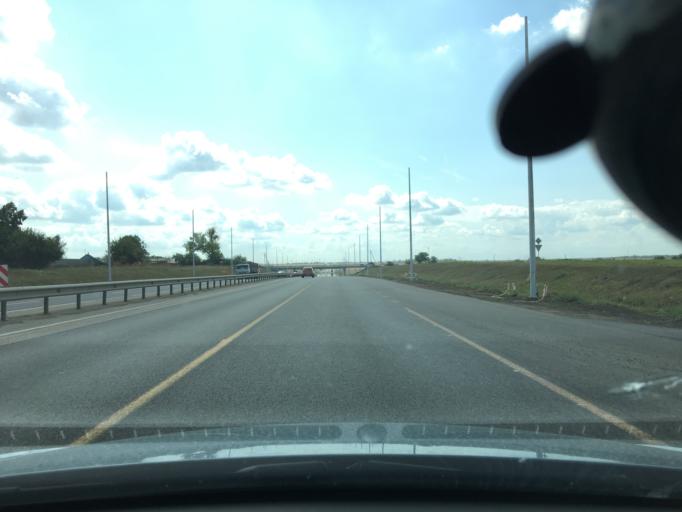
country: RU
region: Krasnodarskiy
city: Berezanskaya
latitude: 45.7376
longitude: 39.6295
